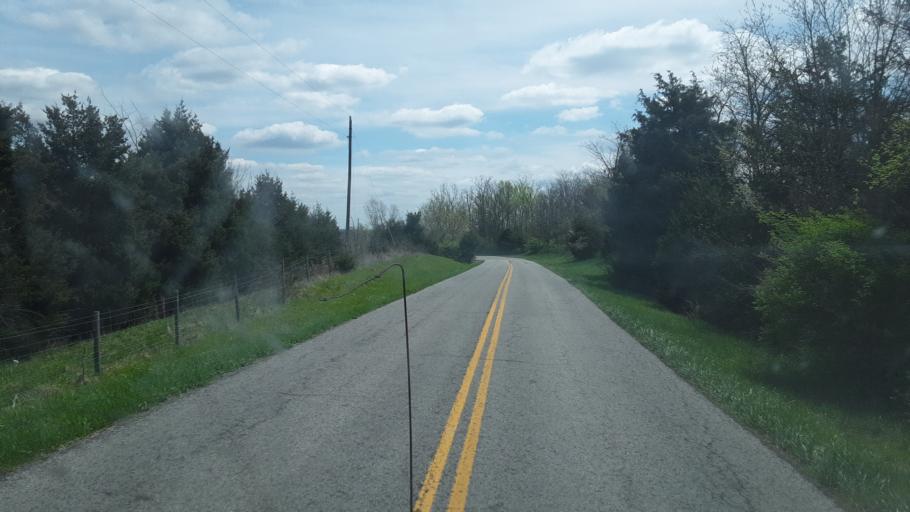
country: US
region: Kentucky
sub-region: Grant County
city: Dry Ridge
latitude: 38.6486
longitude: -84.7374
